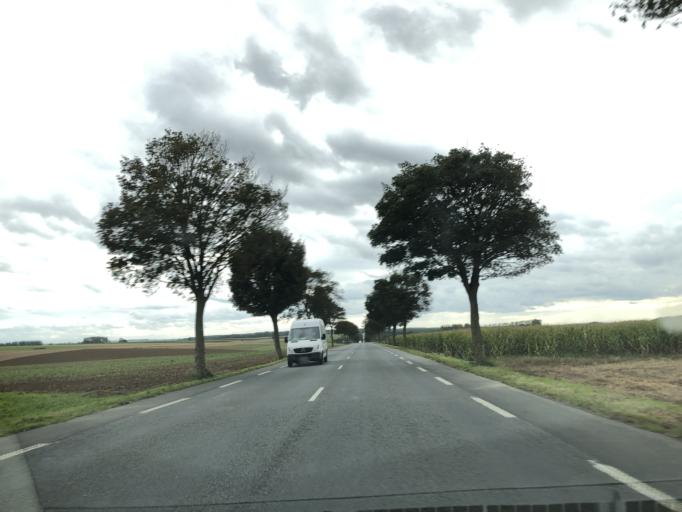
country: FR
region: Nord-Pas-de-Calais
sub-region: Departement du Pas-de-Calais
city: Auchy-les-Hesdin
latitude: 50.4452
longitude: 2.0816
